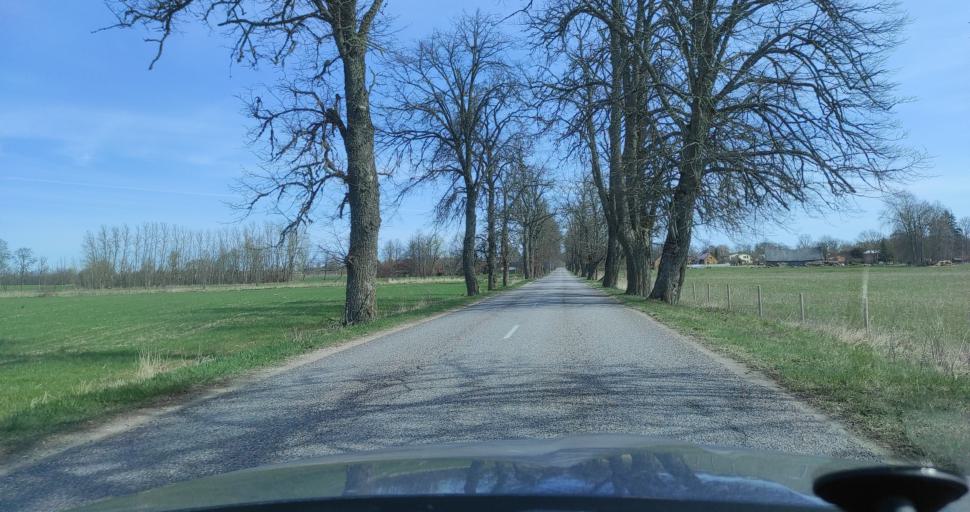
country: LV
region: Talsu Rajons
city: Stende
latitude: 57.2196
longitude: 22.5067
